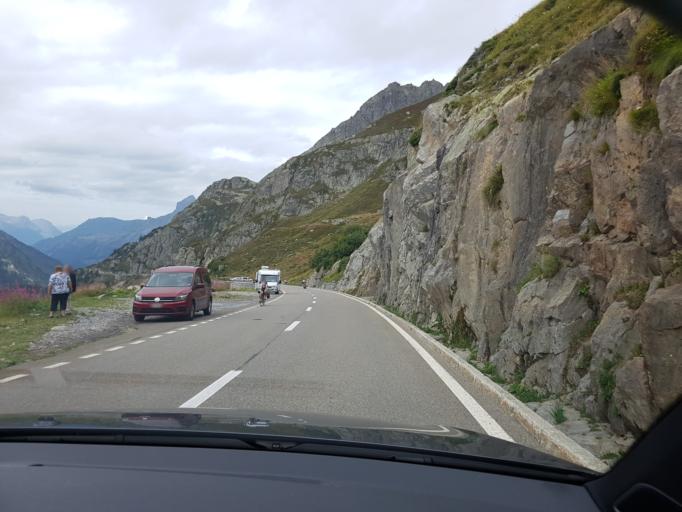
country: CH
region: Obwalden
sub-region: Obwalden
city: Engelberg
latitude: 46.7325
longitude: 8.4354
